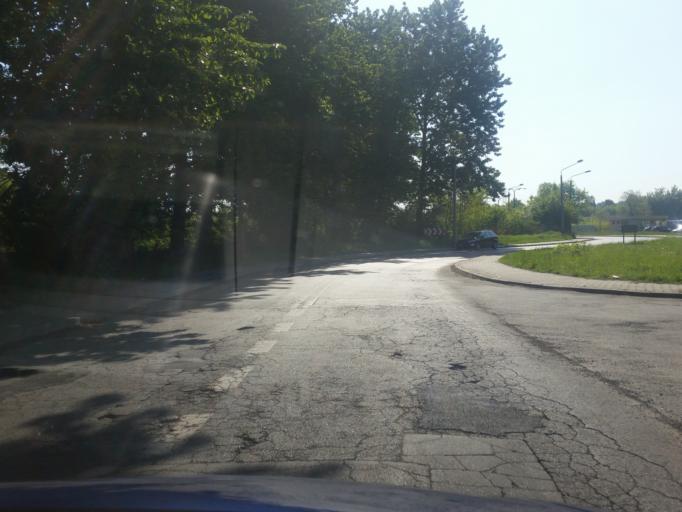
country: PL
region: Silesian Voivodeship
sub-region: Sosnowiec
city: Sosnowiec
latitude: 50.2644
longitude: 19.1330
